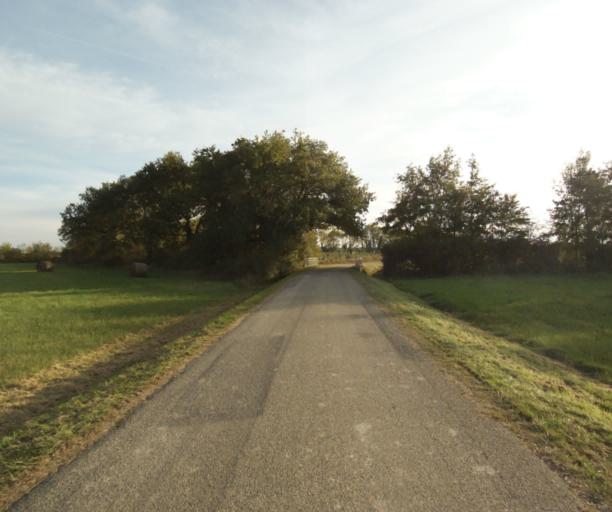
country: FR
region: Midi-Pyrenees
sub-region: Departement du Tarn-et-Garonne
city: Labastide-Saint-Pierre
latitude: 43.8982
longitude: 1.3593
